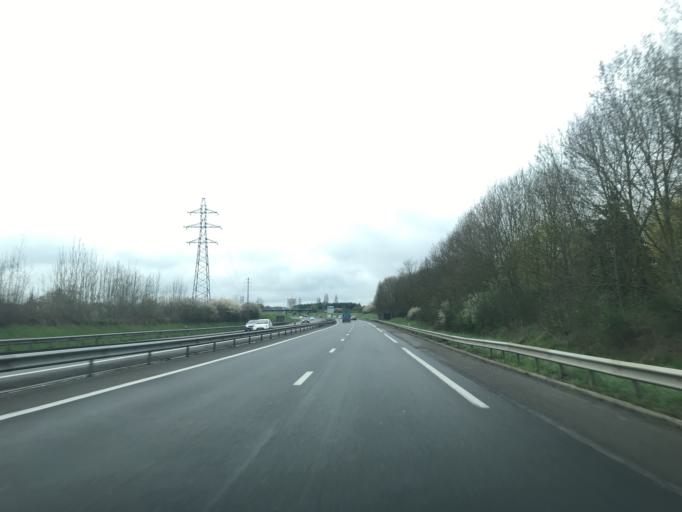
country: FR
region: Centre
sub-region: Departement du Loiret
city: Boigny-sur-Bionne
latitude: 47.9177
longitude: 2.0069
